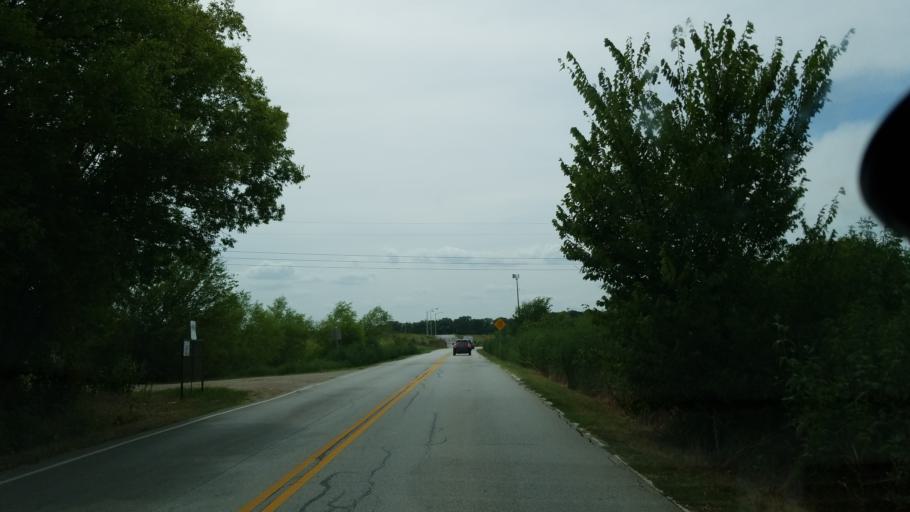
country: US
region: Texas
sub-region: Tarrant County
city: Arlington
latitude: 32.7793
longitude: -97.1381
